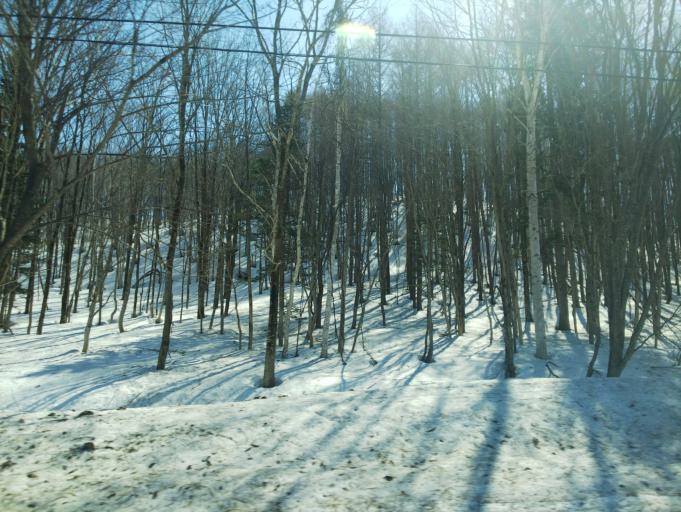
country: JP
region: Hokkaido
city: Nayoro
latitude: 44.6945
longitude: 142.2702
